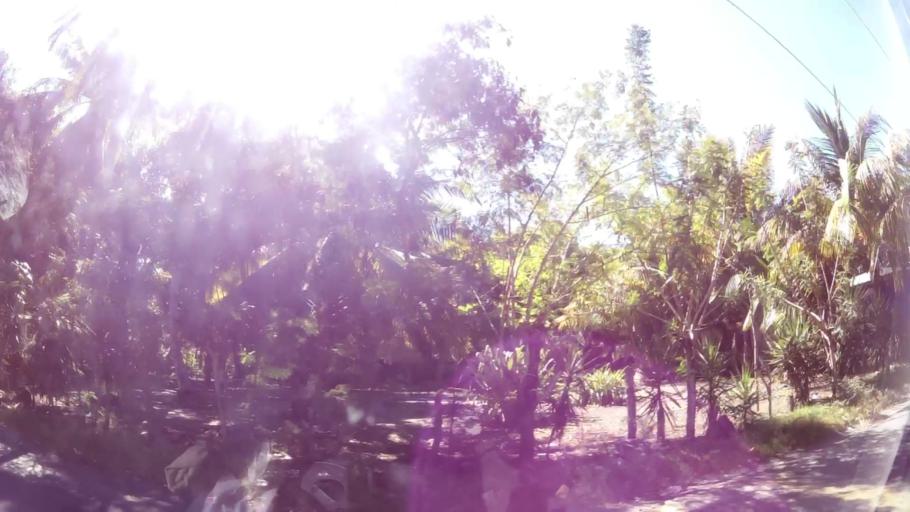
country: GT
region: Escuintla
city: Iztapa
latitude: 13.9334
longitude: -90.6886
